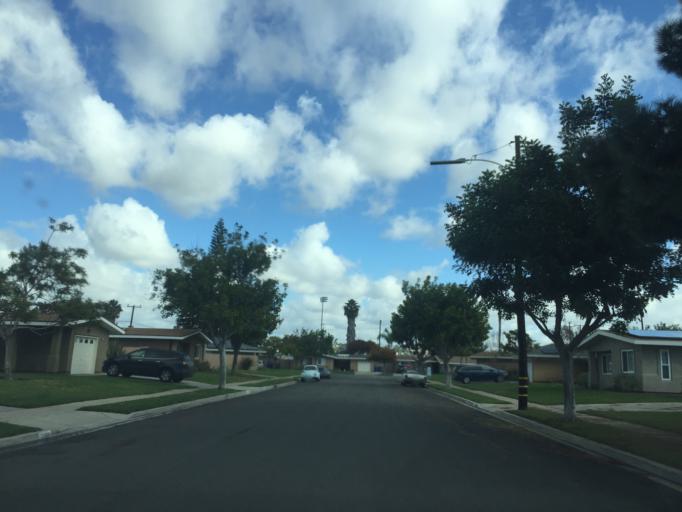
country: US
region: California
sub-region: San Diego County
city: La Jolla
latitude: 32.7981
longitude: -117.2271
